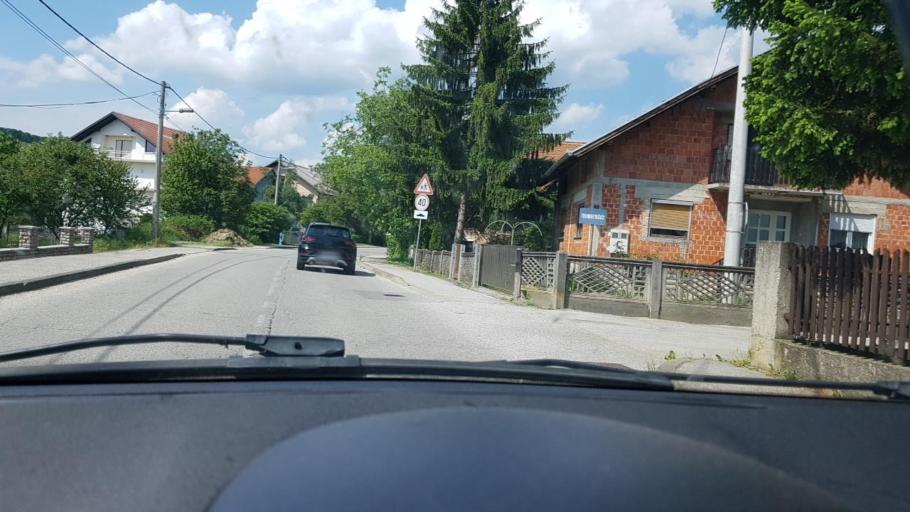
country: HR
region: Grad Zagreb
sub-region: Sesvete
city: Sesvete
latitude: 45.9053
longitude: 16.1634
